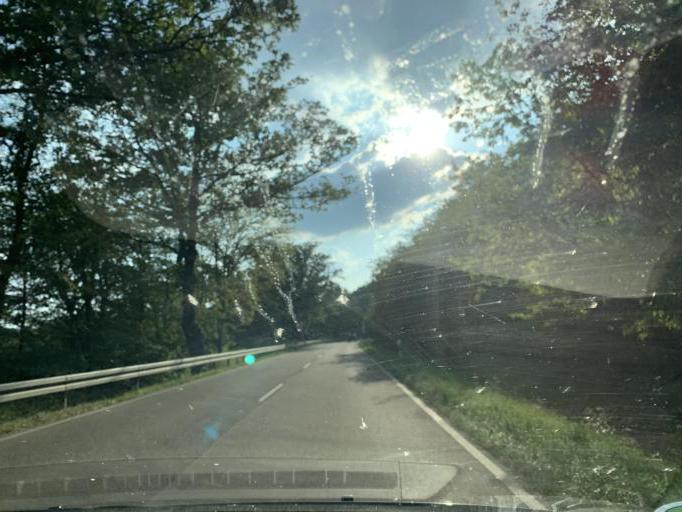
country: DE
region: North Rhine-Westphalia
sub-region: Regierungsbezirk Koln
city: Simmerath
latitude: 50.6248
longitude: 6.3764
